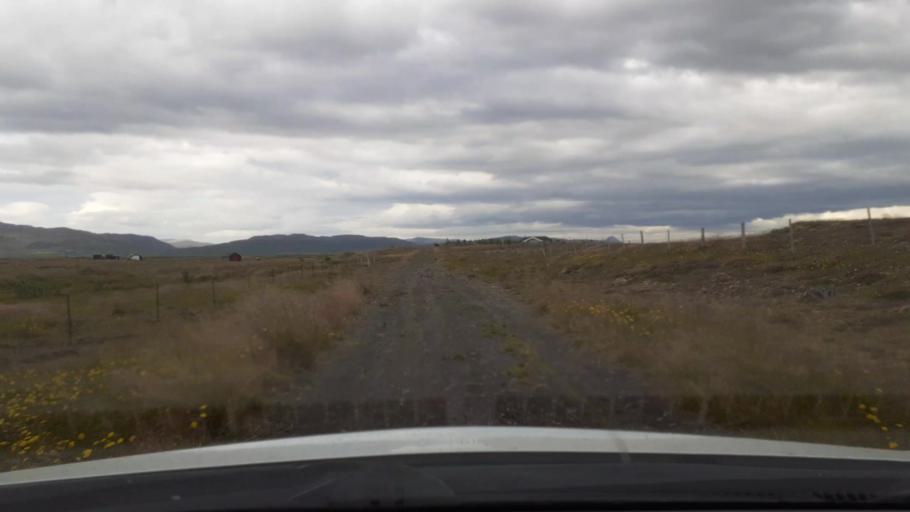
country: IS
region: West
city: Borgarnes
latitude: 64.6552
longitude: -21.8769
